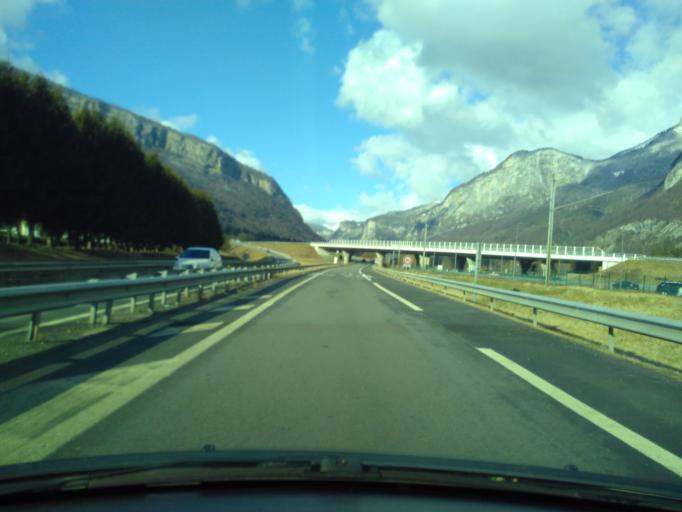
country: FR
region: Rhone-Alpes
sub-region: Departement de la Haute-Savoie
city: Sallanches
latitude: 45.9613
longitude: 6.6296
